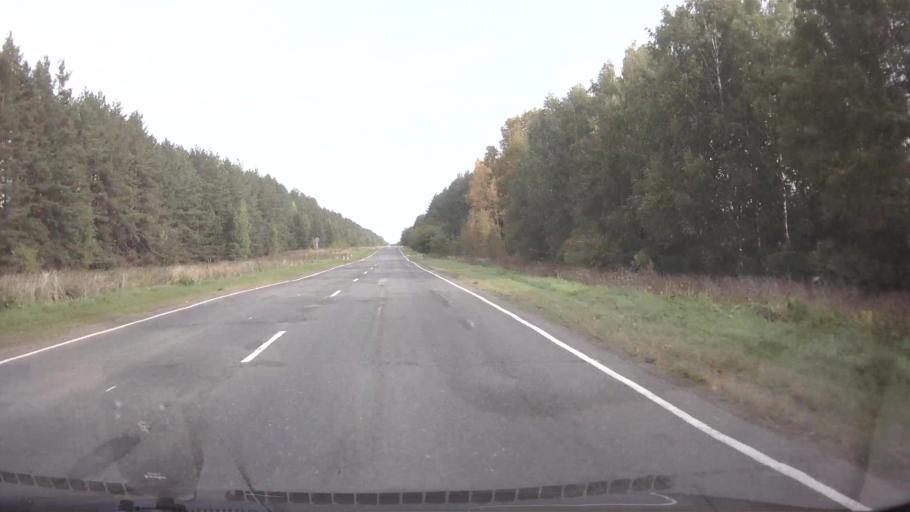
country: RU
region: Mariy-El
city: Kuzhener
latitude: 56.8249
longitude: 48.7220
